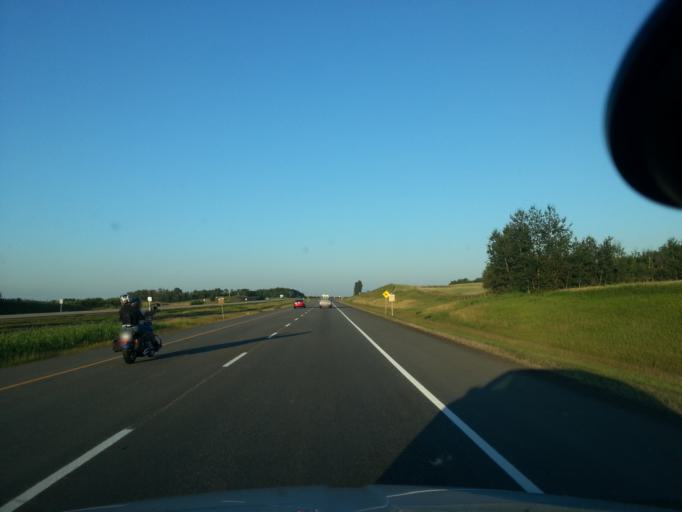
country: CA
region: Alberta
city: Stony Plain
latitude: 53.5712
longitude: -114.0895
